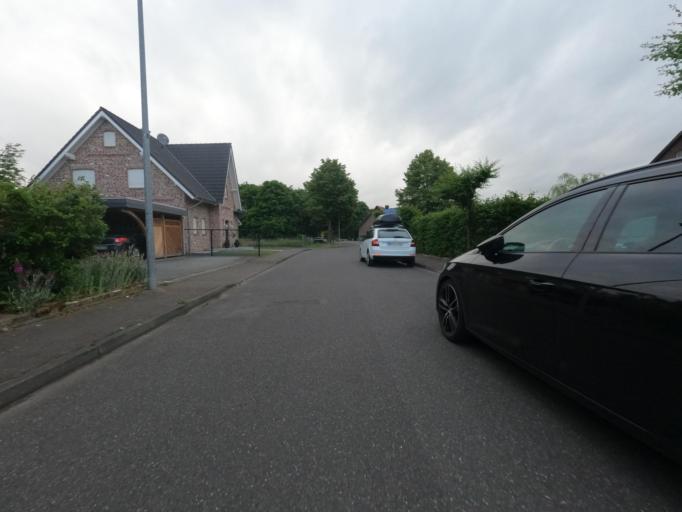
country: NL
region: Limburg
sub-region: Gemeente Roerdalen
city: Vlodrop
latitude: 51.1289
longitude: 6.1053
